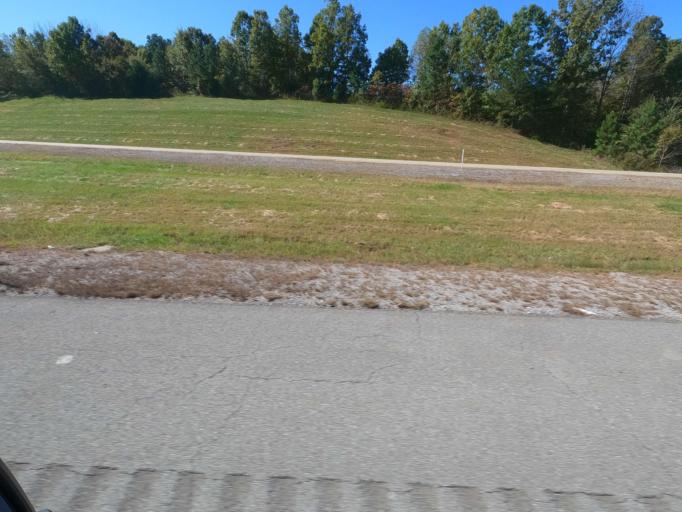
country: US
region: Tennessee
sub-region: Williamson County
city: Fairview
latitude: 35.8809
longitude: -87.1007
